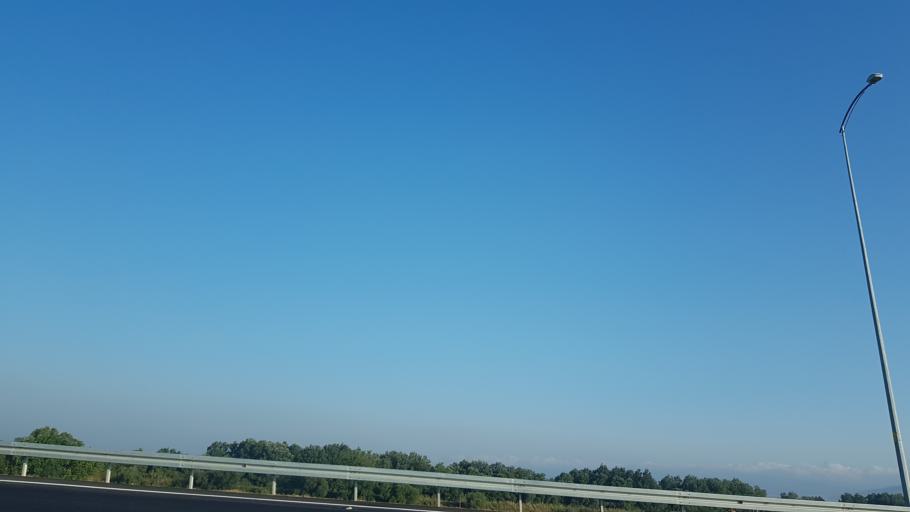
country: TR
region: Bursa
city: Karacabey
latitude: 40.1875
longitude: 28.3377
